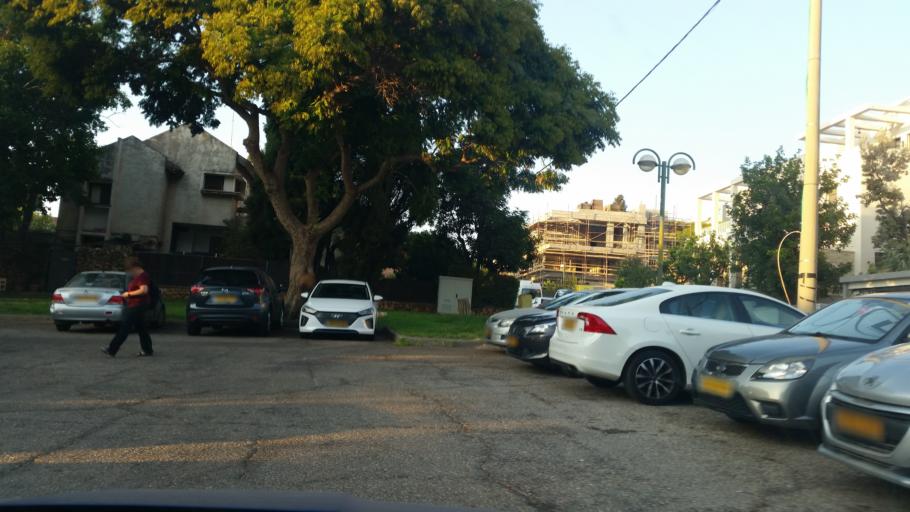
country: IL
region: Tel Aviv
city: Ramat HaSharon
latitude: 32.1478
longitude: 34.8382
